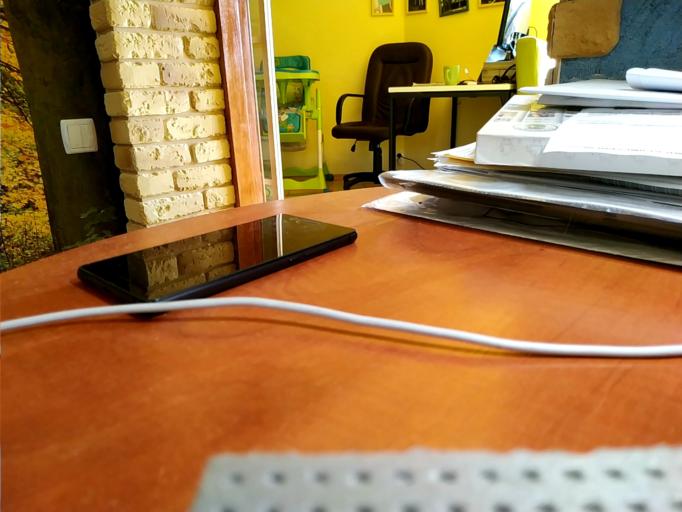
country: RU
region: Tverskaya
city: Kalashnikovo
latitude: 57.3695
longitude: 35.4203
